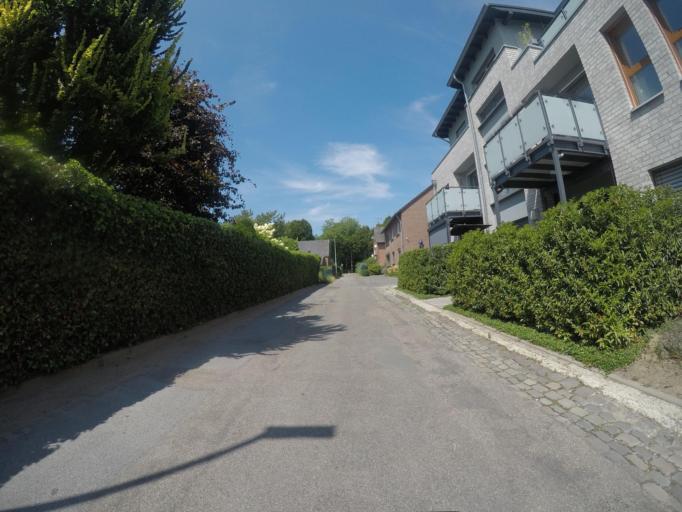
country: DE
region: North Rhine-Westphalia
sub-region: Regierungsbezirk Dusseldorf
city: Kleve
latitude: 51.7750
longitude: 6.1178
